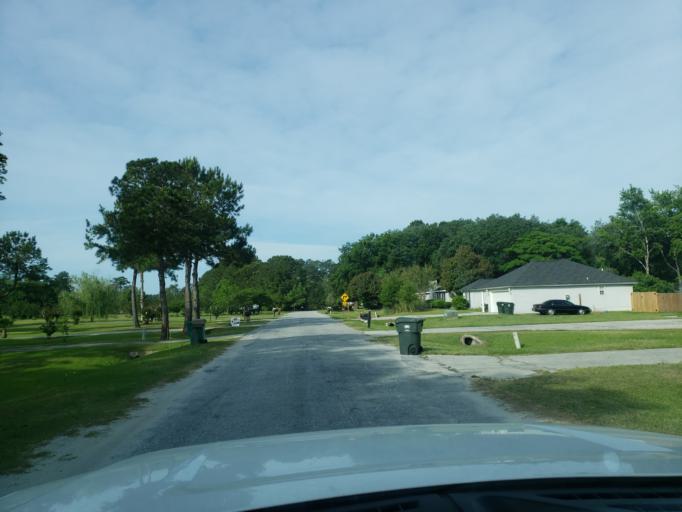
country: US
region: Georgia
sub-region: Chatham County
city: Georgetown
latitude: 32.0038
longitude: -81.2261
